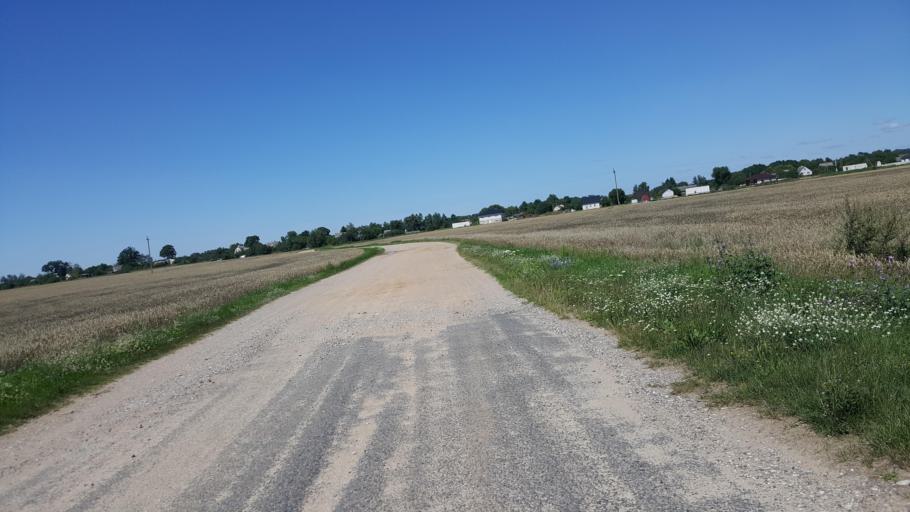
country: BY
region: Brest
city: Charnawchytsy
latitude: 52.2062
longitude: 23.7915
